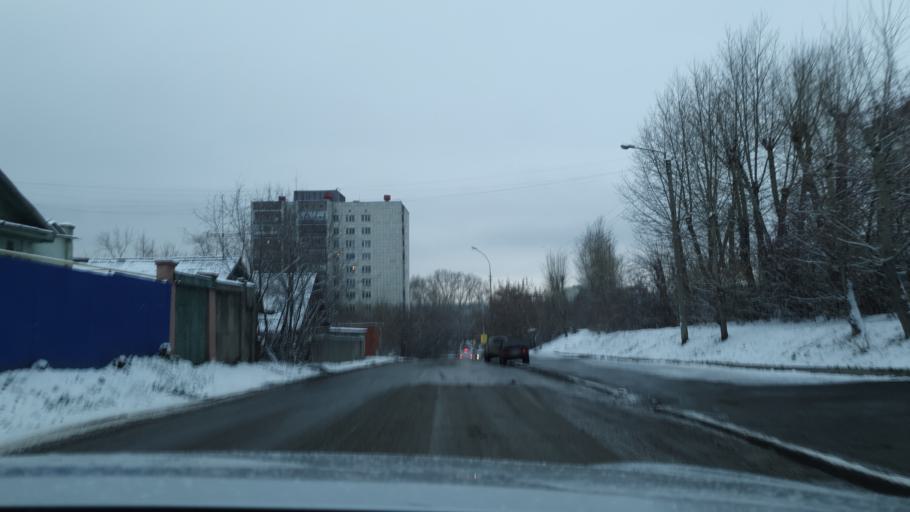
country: RU
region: Sverdlovsk
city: Istok
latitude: 56.7495
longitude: 60.7064
